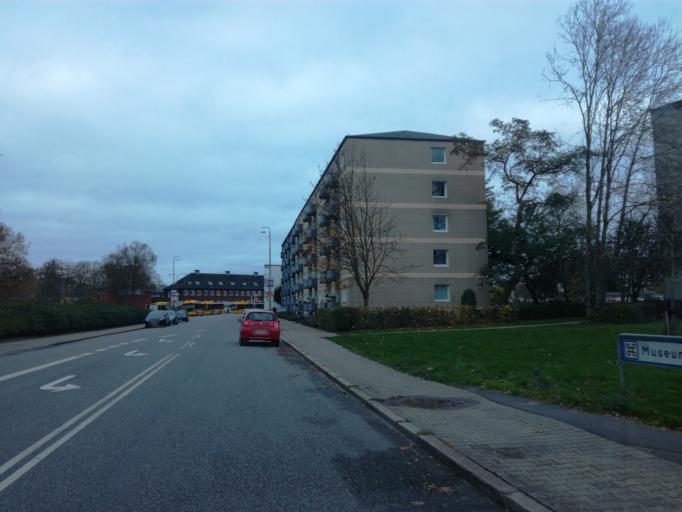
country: DK
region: South Denmark
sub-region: Fredericia Kommune
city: Fredericia
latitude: 55.5667
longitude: 9.7426
